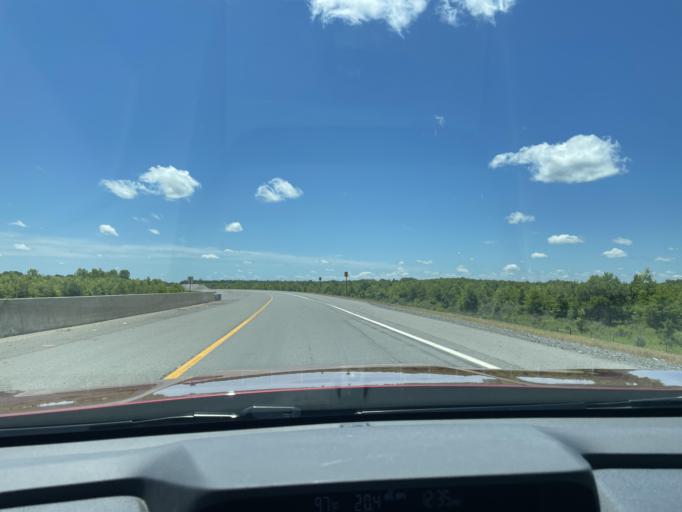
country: US
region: Arkansas
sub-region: Jefferson County
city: Pine Bluff
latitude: 34.1657
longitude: -91.9855
